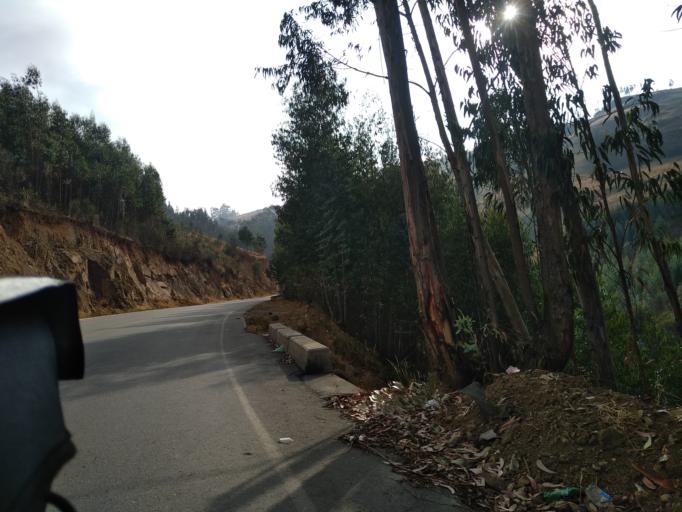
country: PE
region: La Libertad
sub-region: Provincia de Otuzco
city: Agallpampa
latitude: -7.9897
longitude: -78.5326
